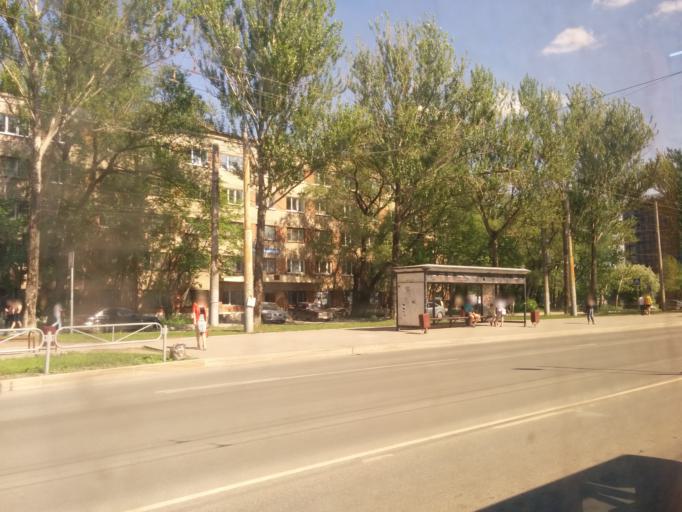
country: RU
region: Perm
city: Perm
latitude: 58.0078
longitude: 56.2833
